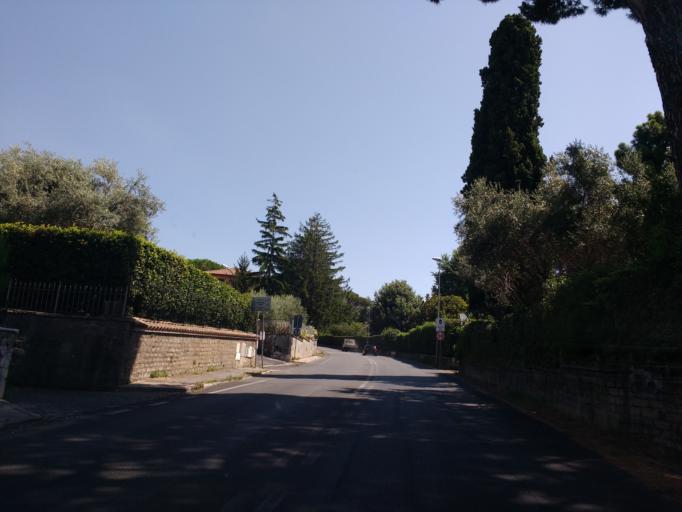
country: IT
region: Latium
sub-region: Citta metropolitana di Roma Capitale
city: Grottaferrata
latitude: 41.7792
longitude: 12.6856
